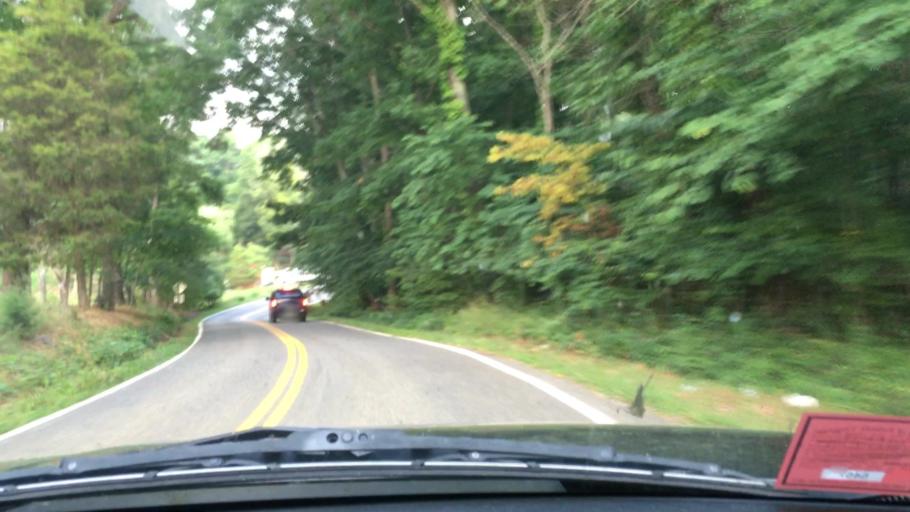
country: US
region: Virginia
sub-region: Pulaski County
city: Dublin
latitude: 37.0560
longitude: -80.6979
